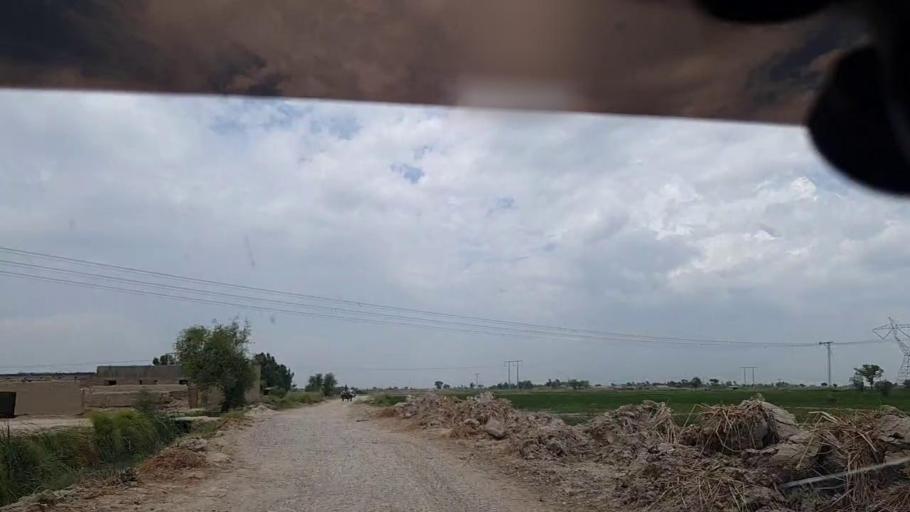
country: PK
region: Sindh
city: Ghauspur
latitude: 28.1090
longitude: 68.9861
